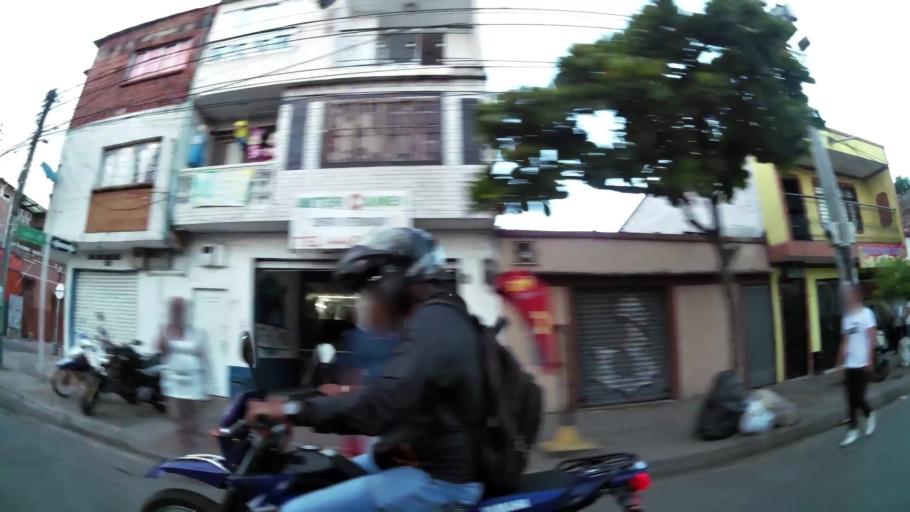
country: CO
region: Valle del Cauca
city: Cali
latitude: 3.4443
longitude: -76.5013
